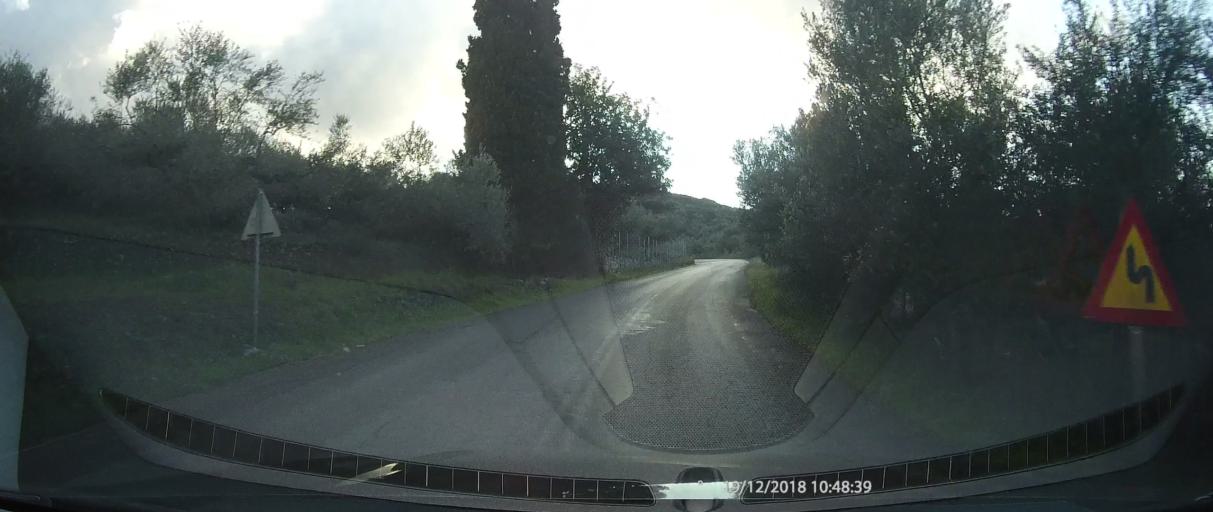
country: GR
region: Peloponnese
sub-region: Nomos Messinias
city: Kardamyli
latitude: 36.9293
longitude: 22.1901
